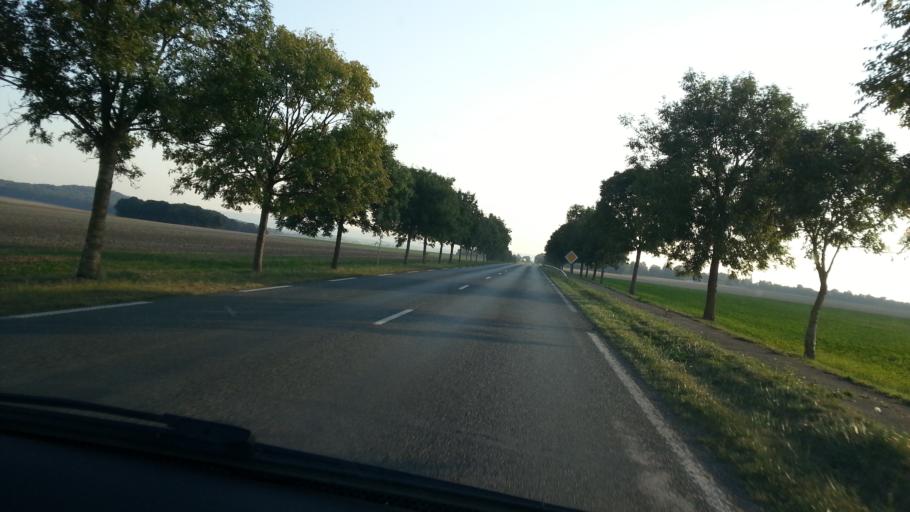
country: FR
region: Picardie
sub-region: Departement de l'Oise
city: Grandfresnoy
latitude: 49.3948
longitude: 2.6235
